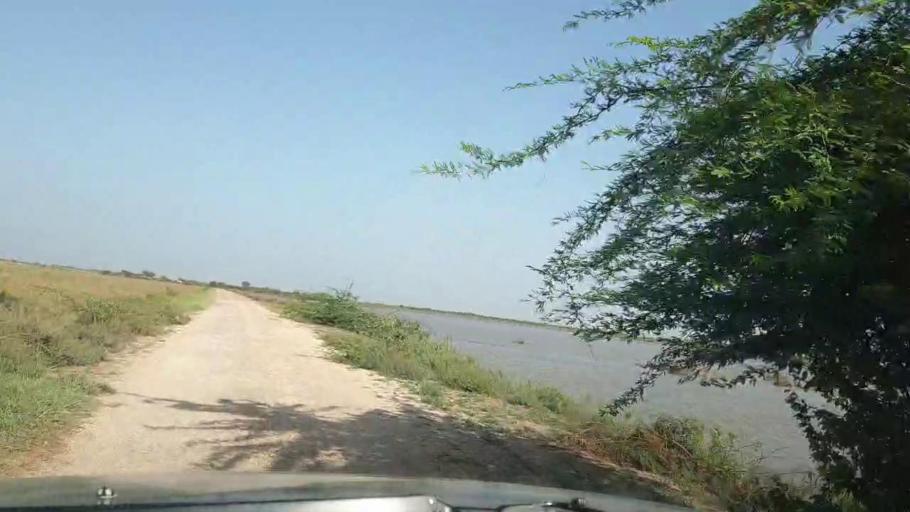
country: PK
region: Sindh
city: Mirwah Gorchani
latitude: 25.2445
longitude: 68.9409
